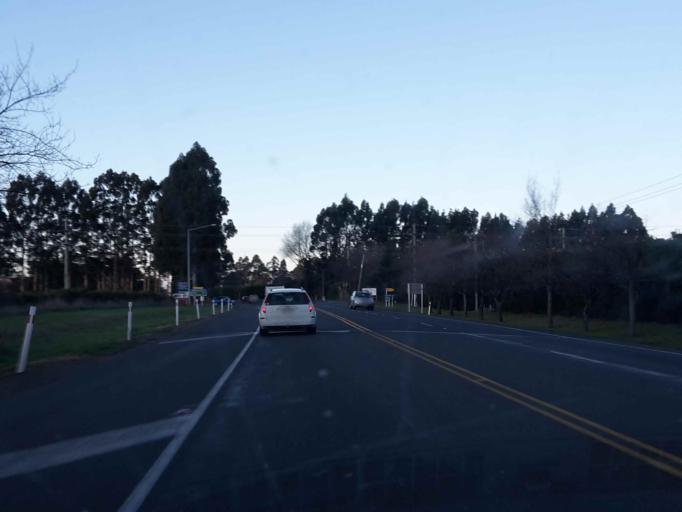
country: NZ
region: Canterbury
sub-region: Selwyn District
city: Rolleston
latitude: -43.5822
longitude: 172.4083
